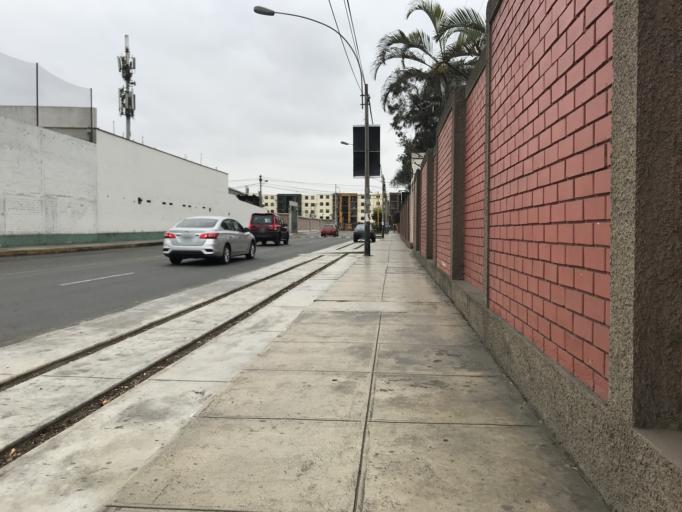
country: PE
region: Callao
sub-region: Callao
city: Callao
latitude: -12.0725
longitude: -77.0758
